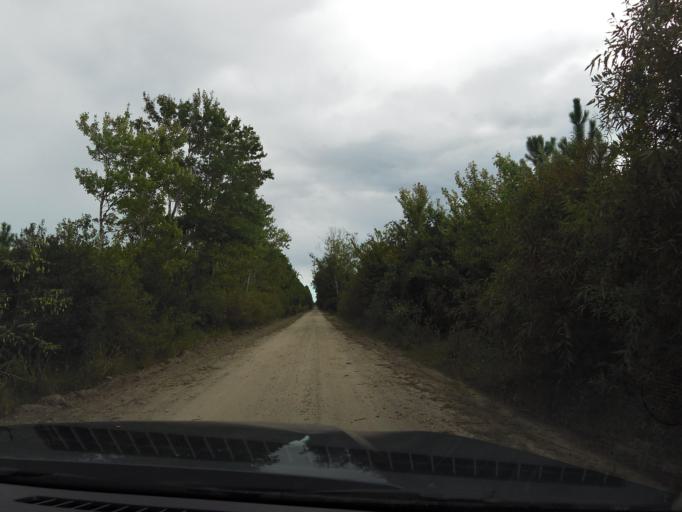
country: US
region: Florida
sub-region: Flagler County
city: Palm Coast
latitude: 29.5796
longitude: -81.3428
